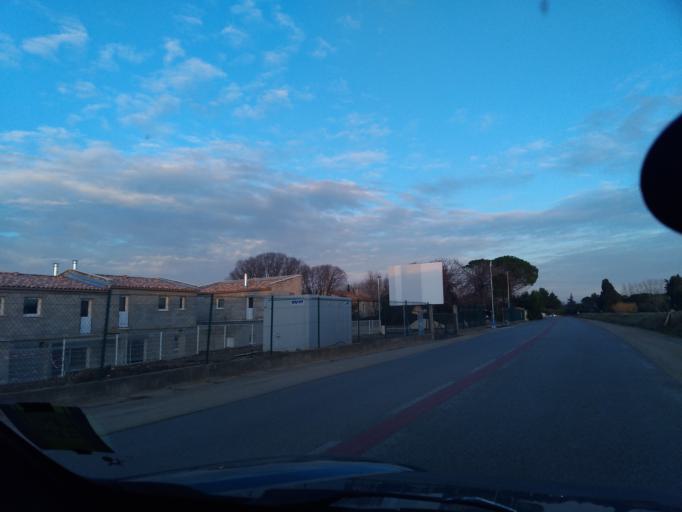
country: FR
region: Provence-Alpes-Cote d'Azur
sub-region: Departement des Bouches-du-Rhone
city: Arles
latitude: 43.6615
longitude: 4.6553
